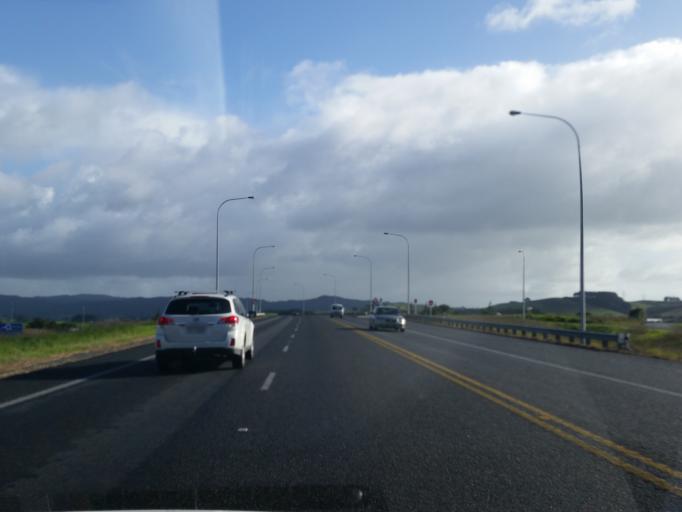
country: NZ
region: Waikato
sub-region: Waikato District
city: Te Kauwhata
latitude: -37.2307
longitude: 175.1623
